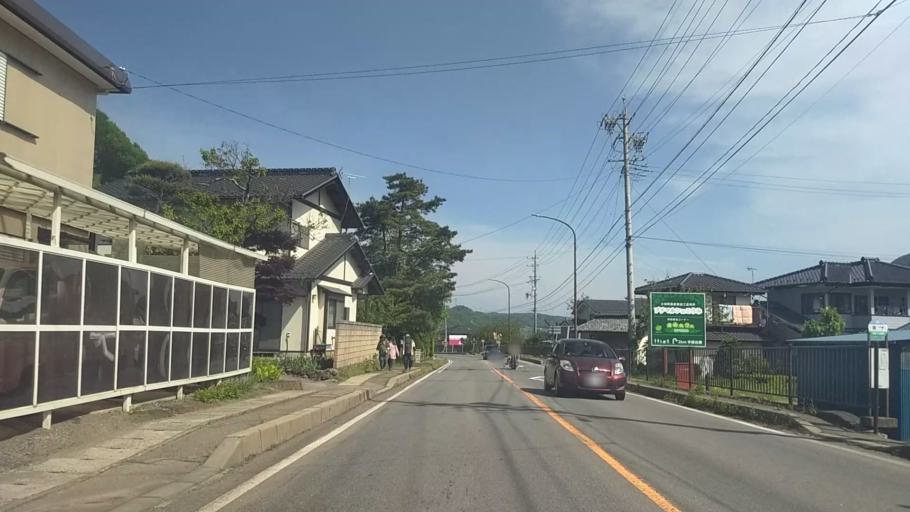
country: JP
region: Nagano
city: Saku
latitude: 36.1092
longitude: 138.4779
